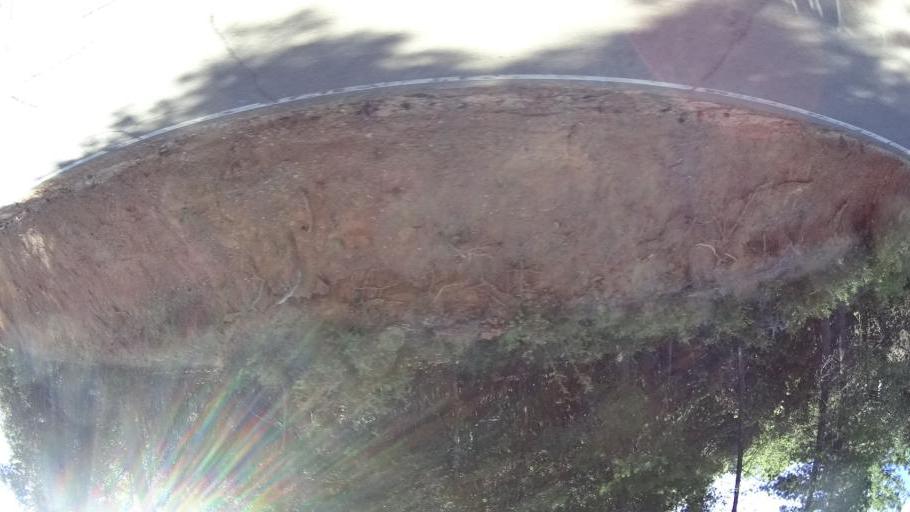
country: US
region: California
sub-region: Amador County
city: Pioneer
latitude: 38.3725
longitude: -120.5073
